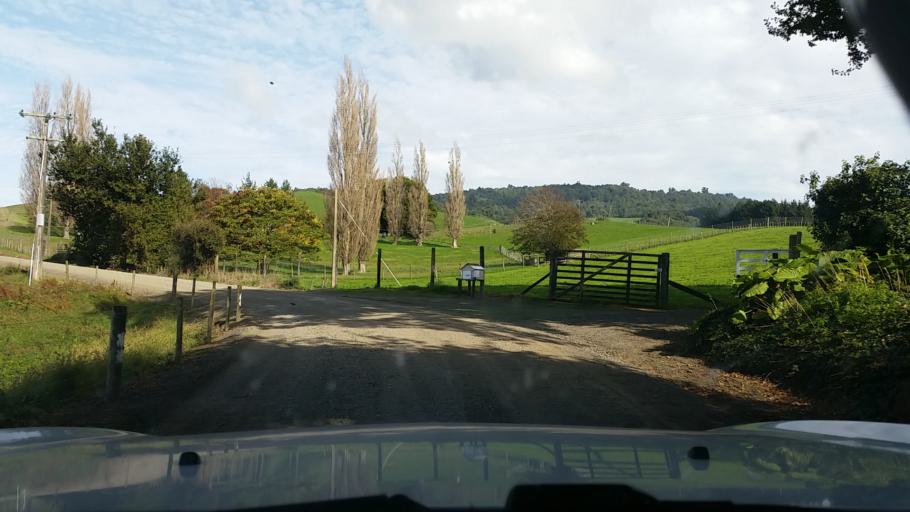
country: NZ
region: Waikato
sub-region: Matamata-Piako District
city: Matamata
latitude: -37.7960
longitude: 175.6326
